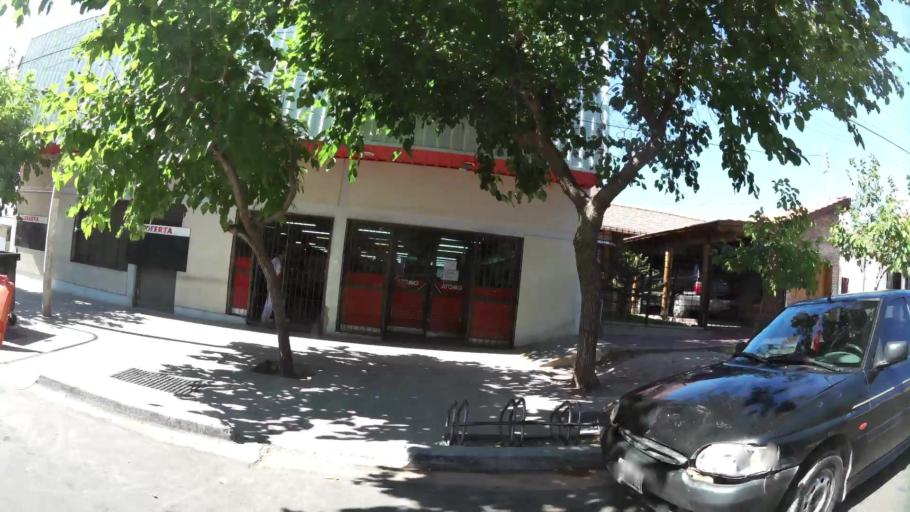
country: AR
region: Mendoza
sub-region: Departamento de Godoy Cruz
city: Godoy Cruz
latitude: -32.9193
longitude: -68.8789
